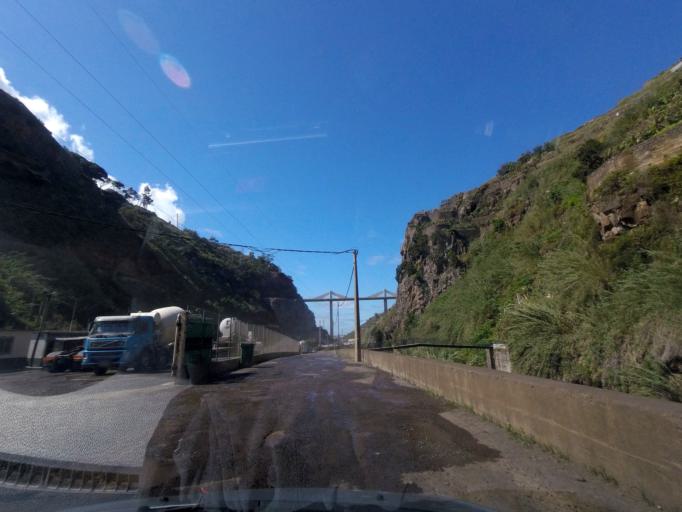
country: PT
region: Madeira
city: Camara de Lobos
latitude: 32.6601
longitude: -16.9616
